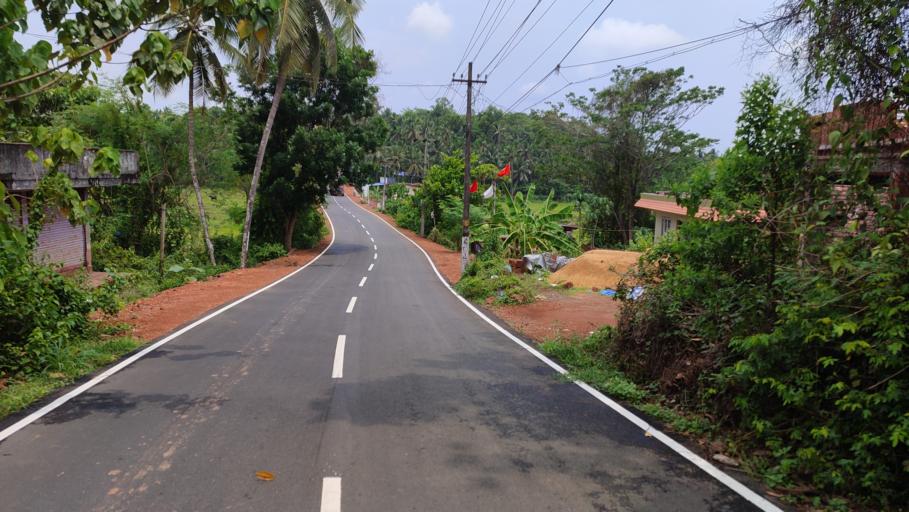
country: IN
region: Kerala
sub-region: Kasaragod District
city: Kannangad
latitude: 12.3178
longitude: 75.1375
